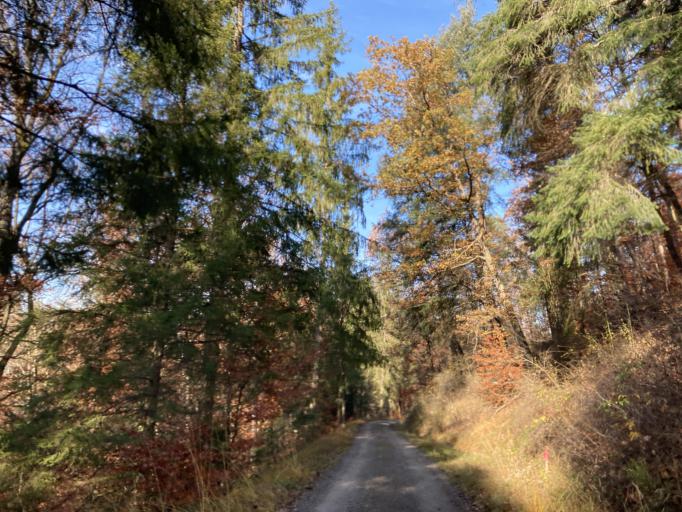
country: DE
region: Baden-Wuerttemberg
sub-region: Regierungsbezirk Stuttgart
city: Altdorf
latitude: 48.5806
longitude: 8.9983
